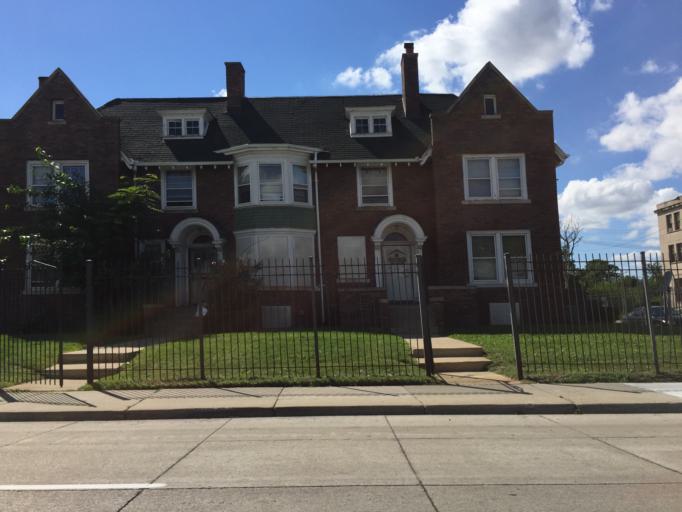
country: US
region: Michigan
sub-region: Wayne County
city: Highland Park
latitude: 42.3803
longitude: -83.0801
